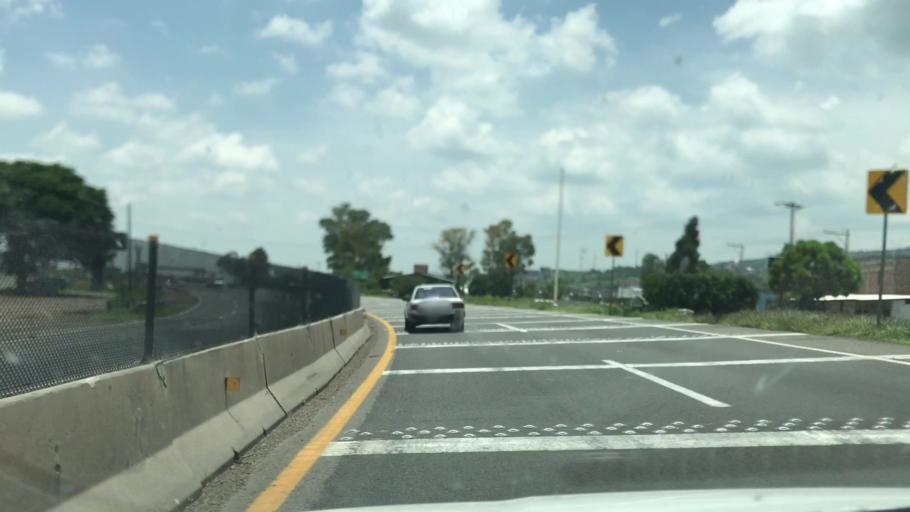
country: MX
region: Guanajuato
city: Abasolo
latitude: 20.4506
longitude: -101.5520
